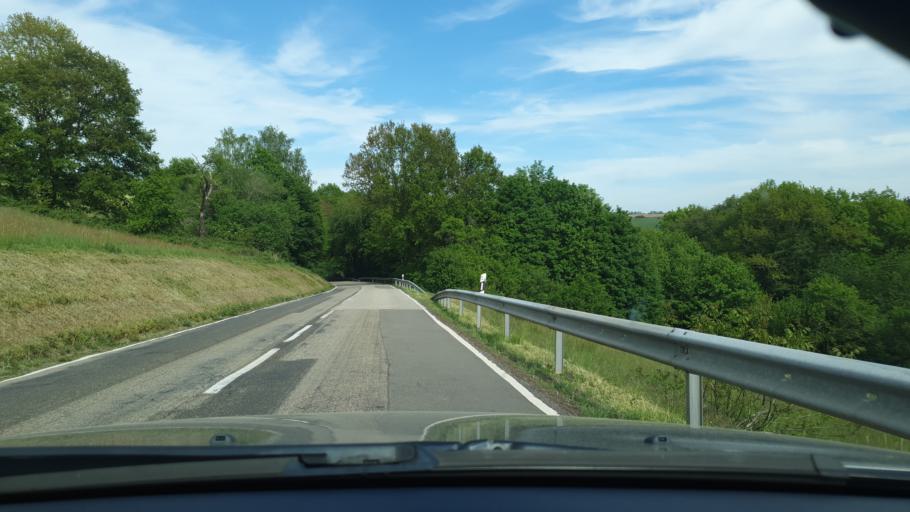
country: DE
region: Rheinland-Pfalz
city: Knopp-Labach
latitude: 49.3191
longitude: 7.5067
